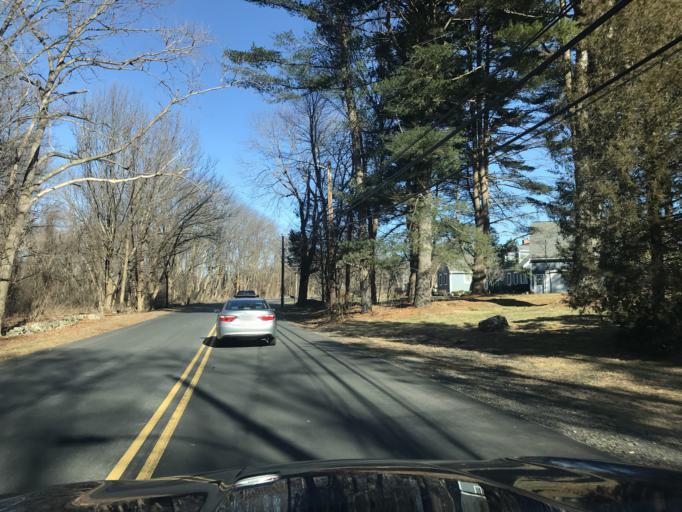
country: US
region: Massachusetts
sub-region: Essex County
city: Groveland
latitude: 42.7148
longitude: -71.0168
